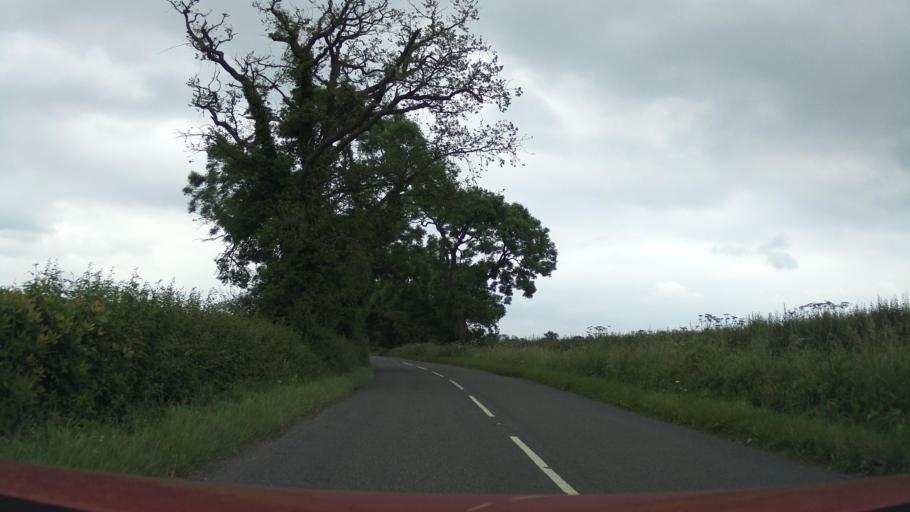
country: GB
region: England
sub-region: Derbyshire
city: Rodsley
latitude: 52.8735
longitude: -1.7295
